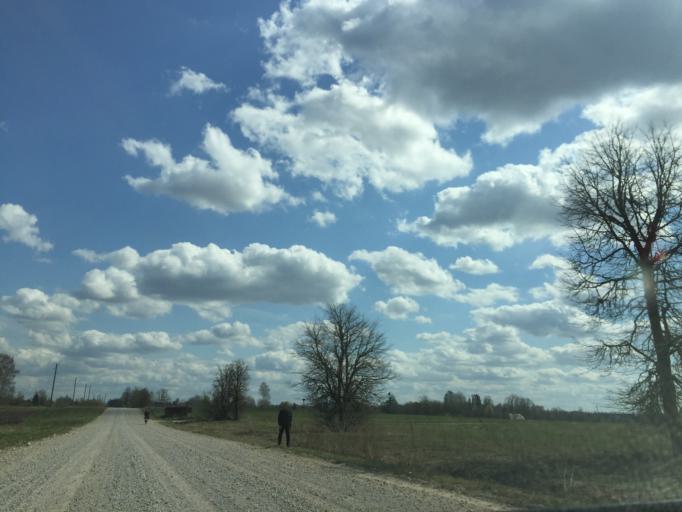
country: LV
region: Ogre
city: Jumprava
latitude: 56.7579
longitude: 25.0518
